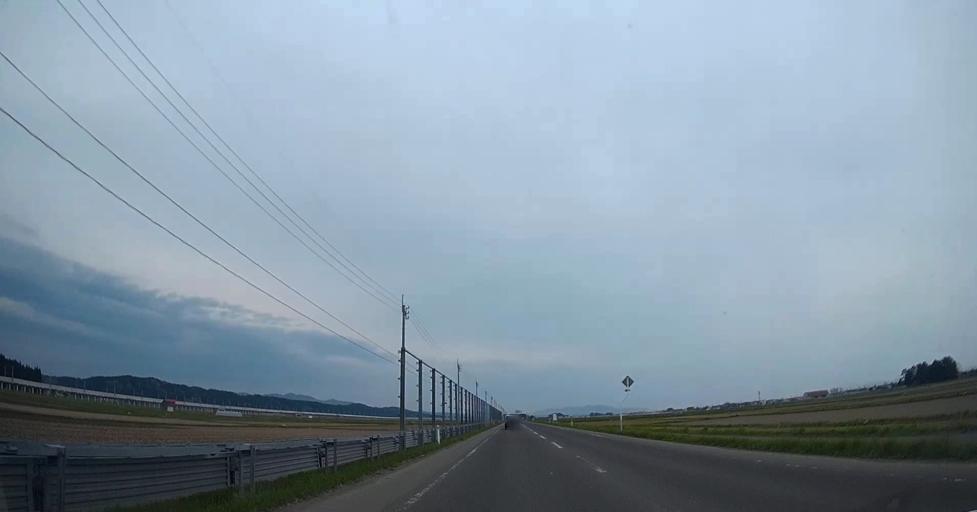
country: JP
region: Aomori
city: Aomori Shi
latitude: 40.8704
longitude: 140.6753
